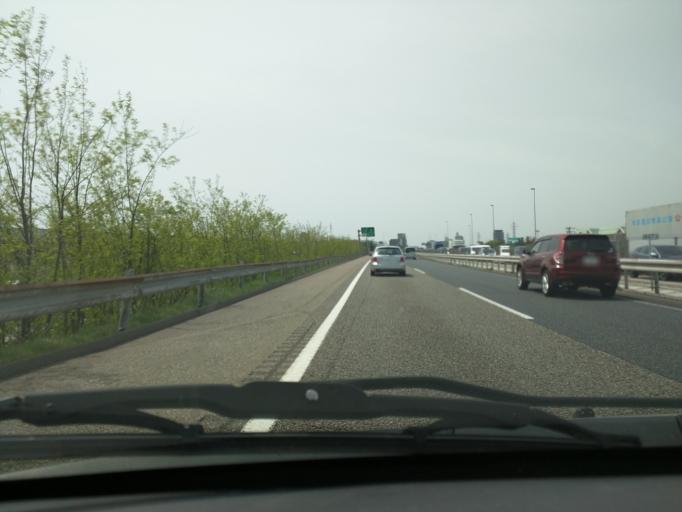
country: JP
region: Niigata
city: Tsubame
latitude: 37.6566
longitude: 138.9420
